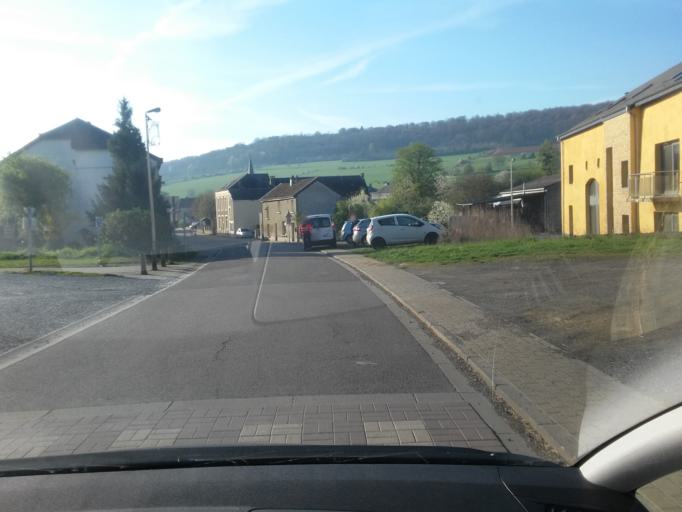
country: BE
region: Wallonia
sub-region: Province du Luxembourg
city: Rouvroy
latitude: 49.5281
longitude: 5.4775
